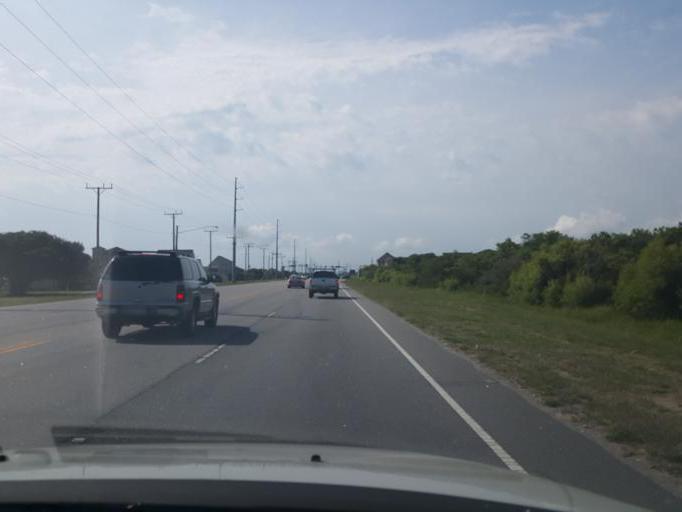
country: US
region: North Carolina
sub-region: Dare County
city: Kill Devil Hills
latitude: 36.0163
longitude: -75.6626
